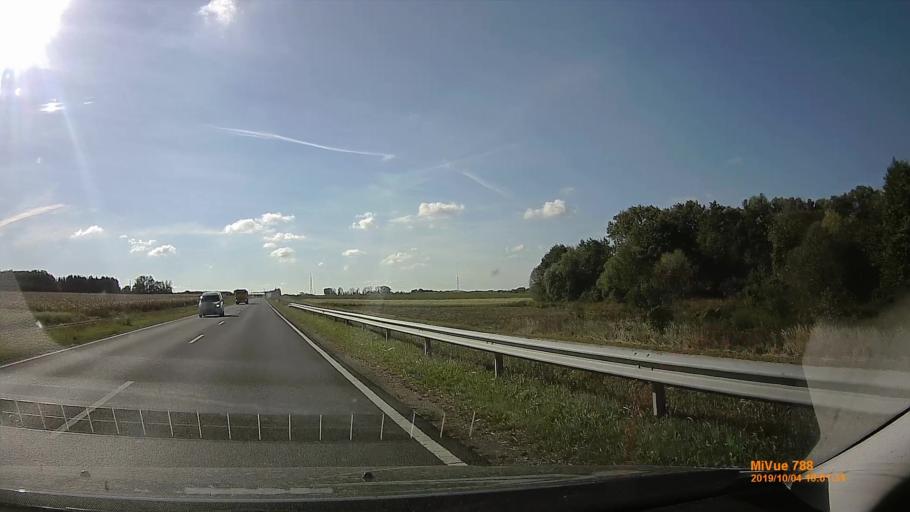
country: HU
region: Somogy
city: Kaposvar
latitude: 46.4062
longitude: 17.7730
